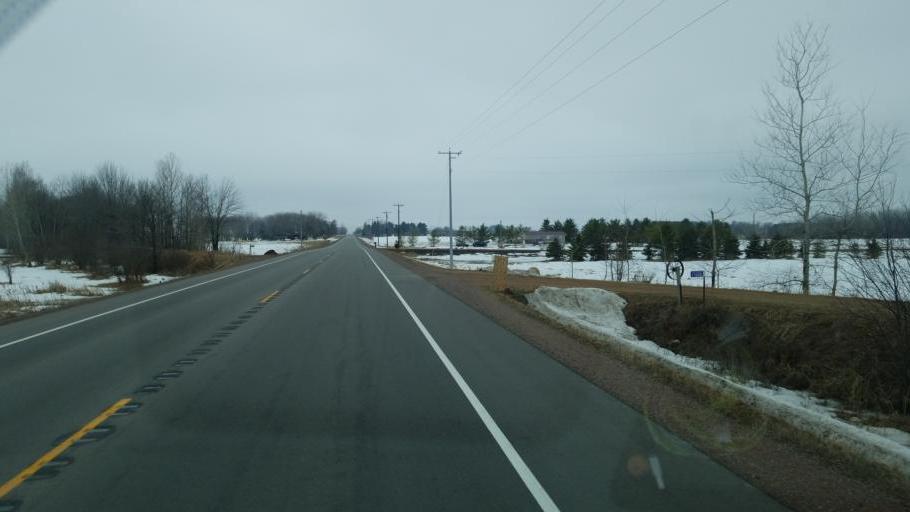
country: US
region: Wisconsin
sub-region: Wood County
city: Marshfield
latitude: 44.6564
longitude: -90.2678
